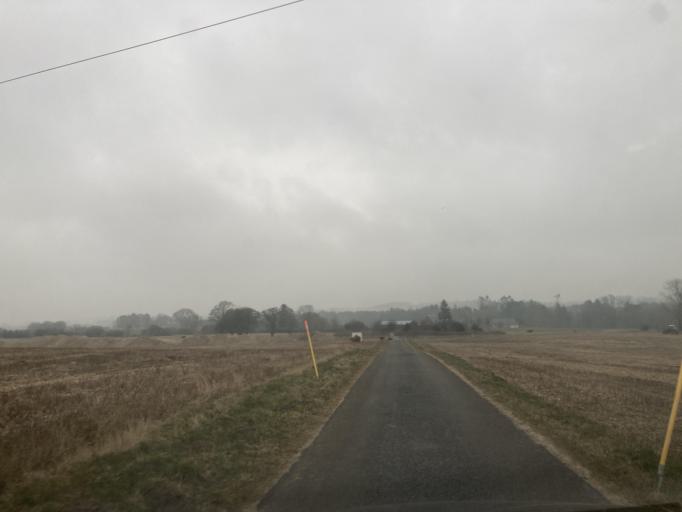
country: DK
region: Zealand
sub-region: Vordingborg Kommune
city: Orslev
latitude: 55.1559
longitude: 11.9103
